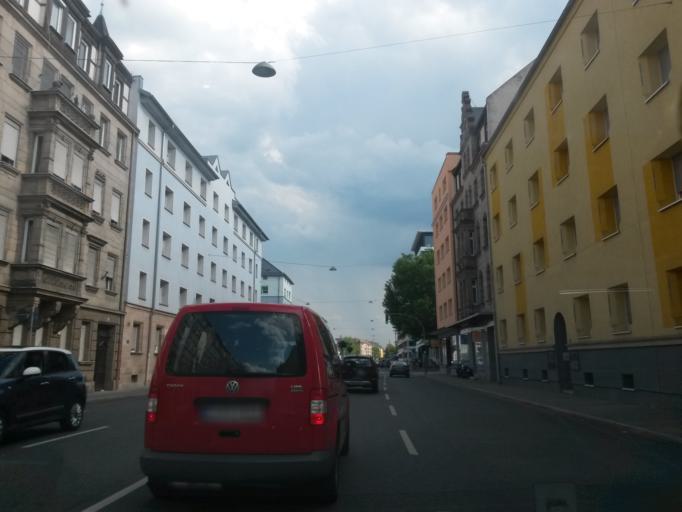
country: DE
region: Bavaria
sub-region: Regierungsbezirk Mittelfranken
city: Furth
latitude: 49.4630
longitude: 10.9864
